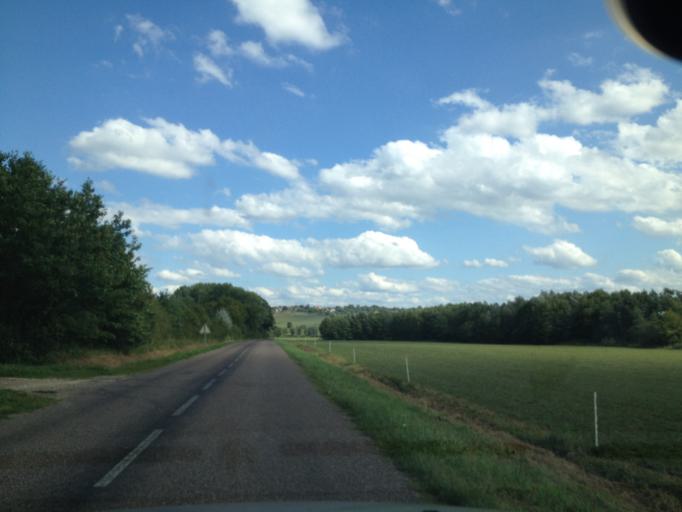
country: FR
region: Franche-Comte
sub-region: Departement de la Haute-Saone
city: Saint-Loup-sur-Semouse
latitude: 47.8581
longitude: 6.1944
